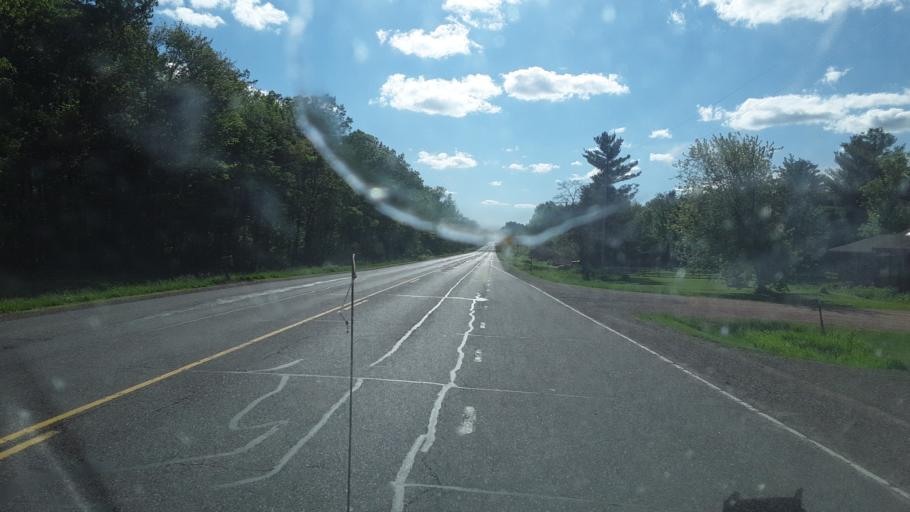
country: US
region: Wisconsin
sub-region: Wood County
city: Marshfield
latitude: 44.4536
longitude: -90.1614
